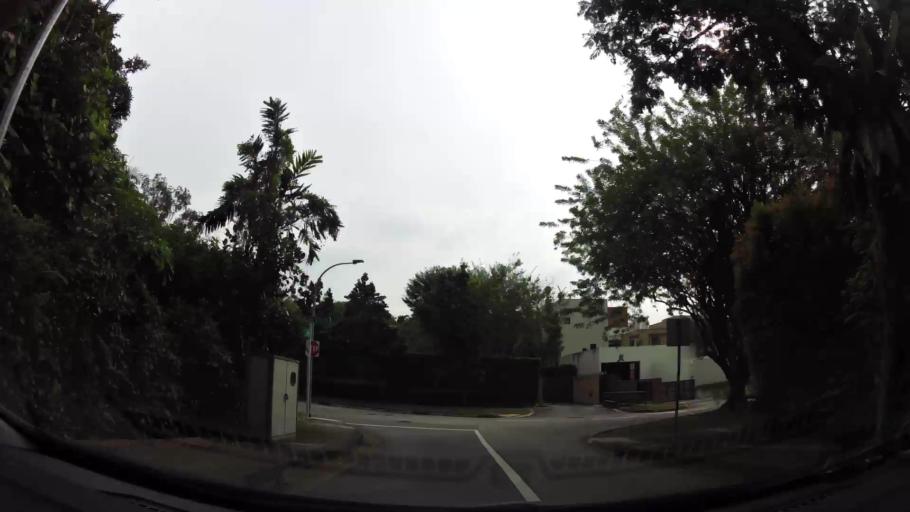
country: SG
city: Singapore
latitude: 1.3178
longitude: 103.7972
